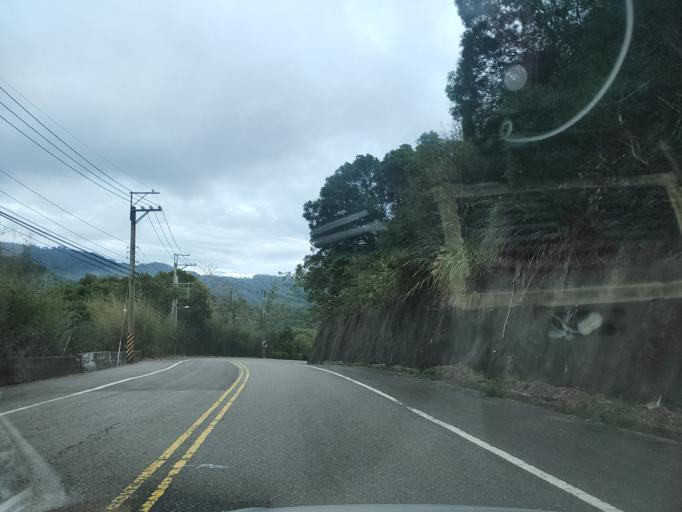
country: TW
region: Taiwan
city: Fengyuan
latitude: 24.3675
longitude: 120.7757
